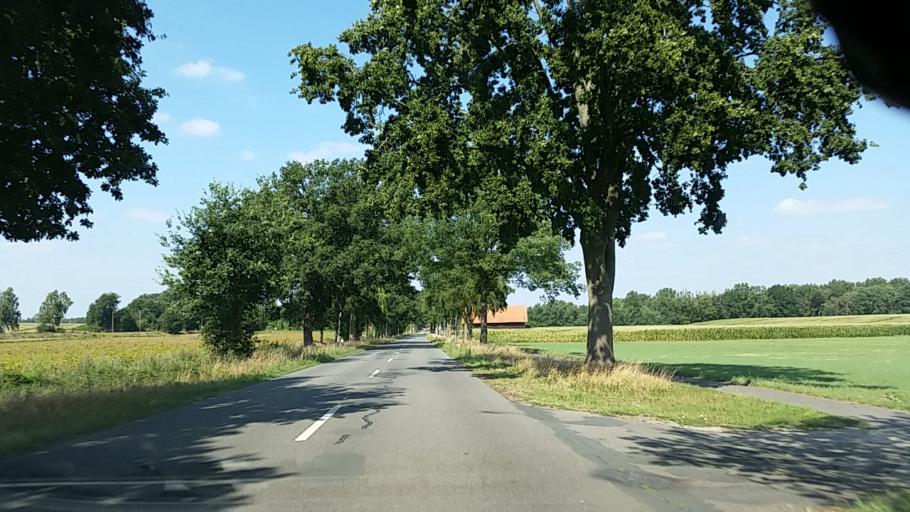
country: DE
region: Lower Saxony
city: Bad Bevensen
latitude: 53.0978
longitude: 10.5568
